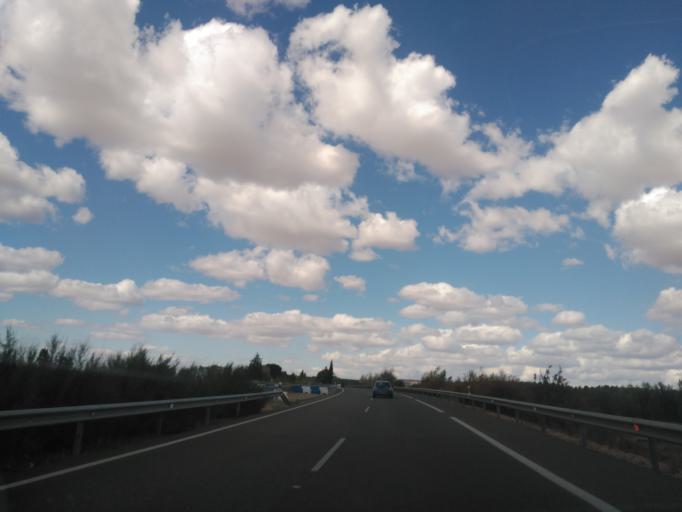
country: ES
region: Castille and Leon
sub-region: Provincia de Palencia
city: Venta de Banos
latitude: 41.9288
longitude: -4.4987
